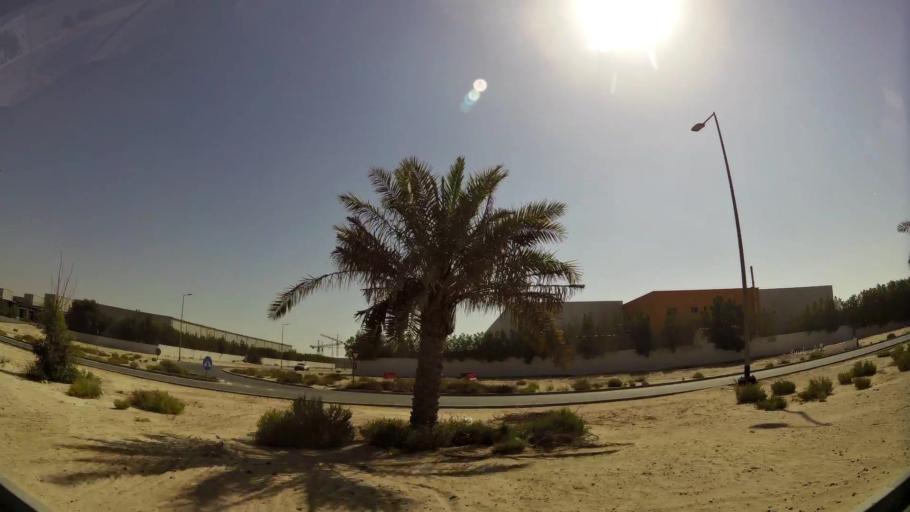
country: AE
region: Dubai
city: Dubai
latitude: 24.9310
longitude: 55.0548
